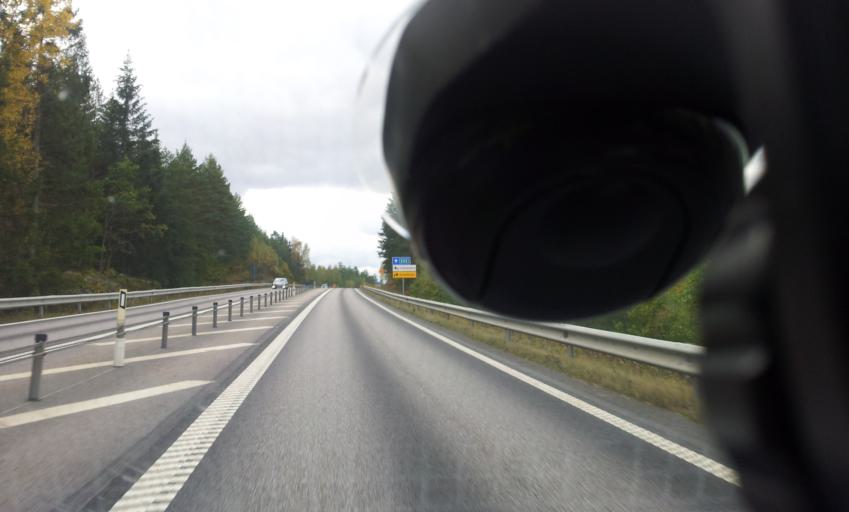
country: SE
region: Kalmar
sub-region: Vasterviks Kommun
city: Forserum
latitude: 58.0170
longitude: 16.5157
